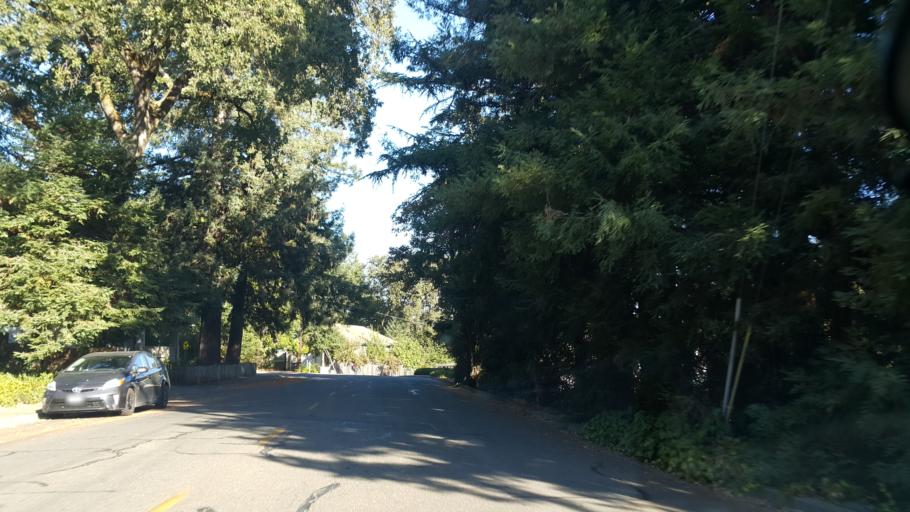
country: US
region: California
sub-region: Mendocino County
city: Ukiah
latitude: 39.1543
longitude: -123.2141
